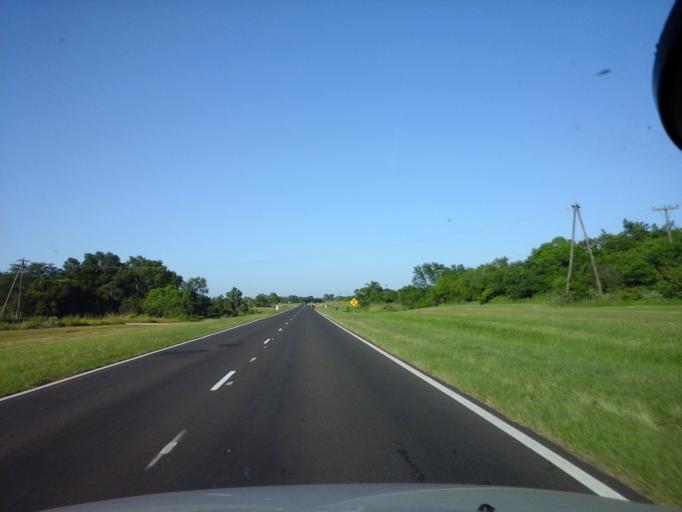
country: AR
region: Corrientes
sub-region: Departamento de Beron de Astrada
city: Beron de Astrada
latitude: -27.4666
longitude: -57.4715
